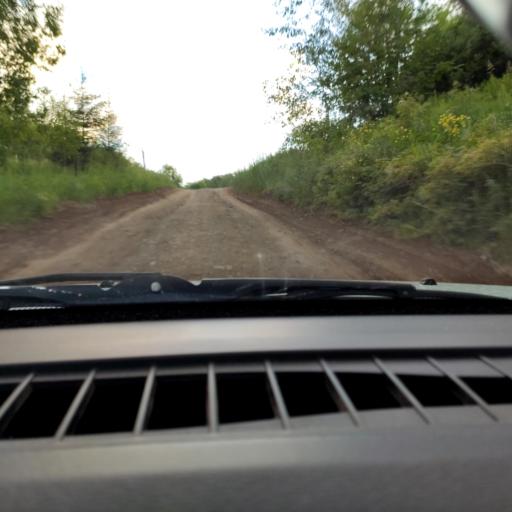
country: RU
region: Perm
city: Polazna
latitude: 58.1914
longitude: 56.4800
